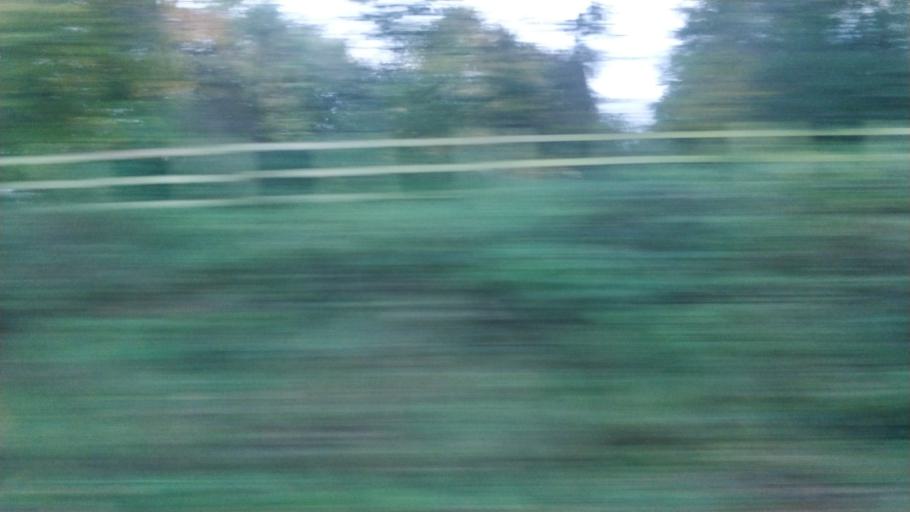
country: GB
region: England
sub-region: Lancashire
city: Parbold
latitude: 53.5949
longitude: -2.7908
